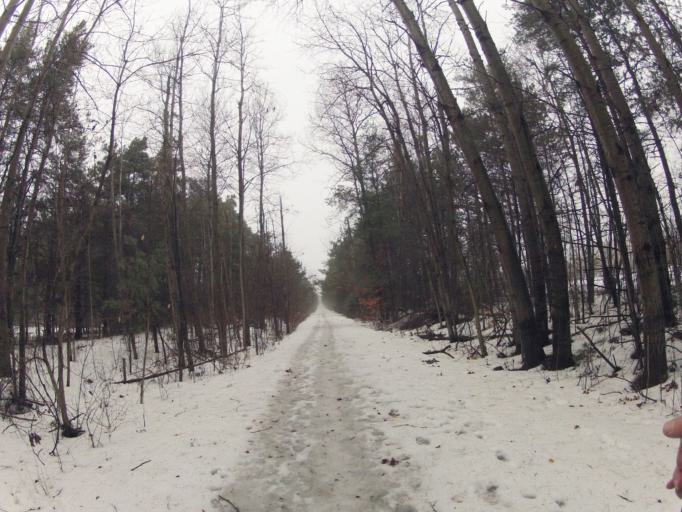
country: CA
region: Ontario
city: Brampton
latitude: 43.8375
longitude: -79.8903
